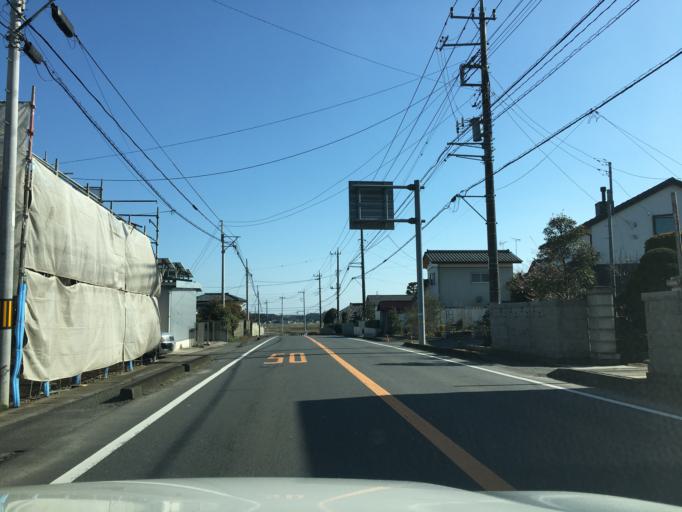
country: JP
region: Ibaraki
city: Omiya
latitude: 36.5141
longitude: 140.3668
